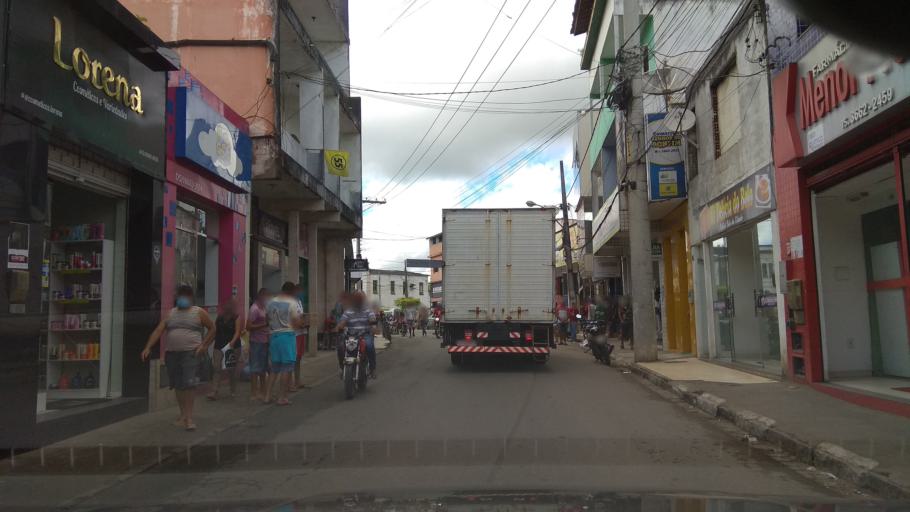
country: BR
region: Bahia
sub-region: Mutuipe
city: Mutuipe
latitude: -13.1833
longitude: -39.4233
